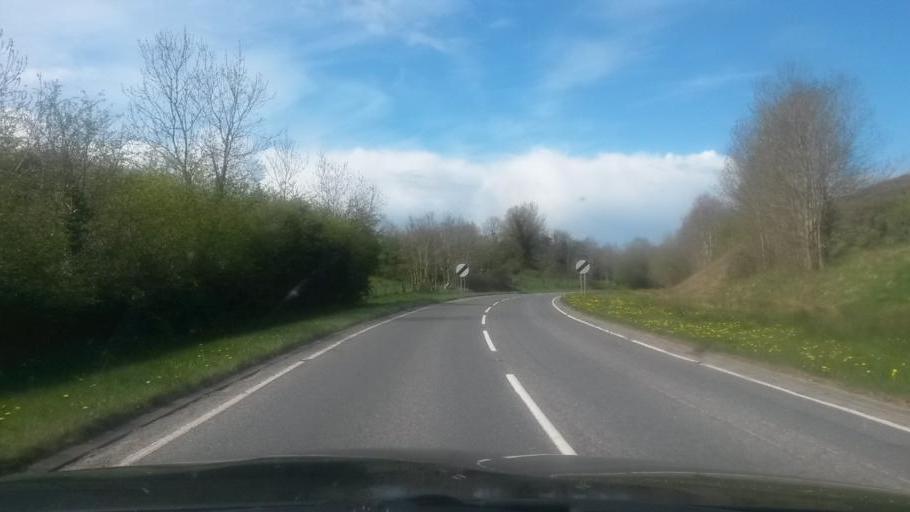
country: GB
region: Northern Ireland
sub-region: Fermanagh District
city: Enniskillen
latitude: 54.3622
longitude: -7.6775
